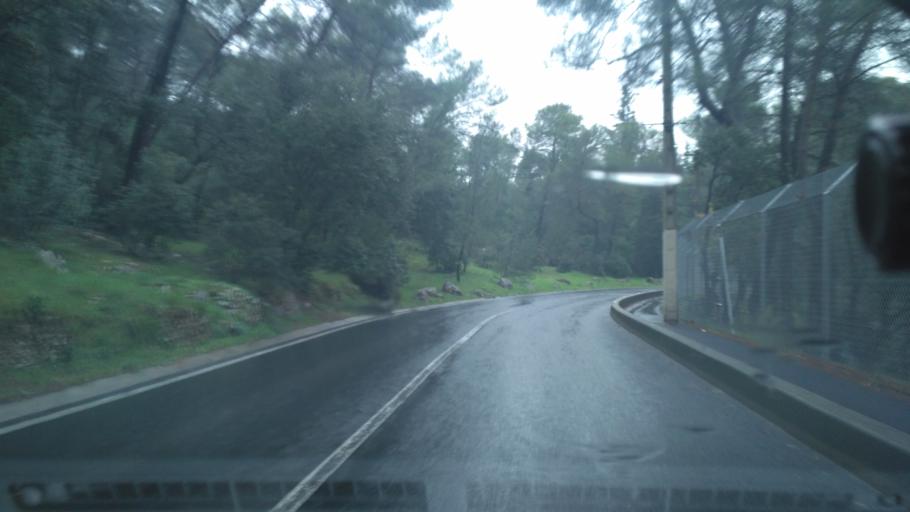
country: FR
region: Languedoc-Roussillon
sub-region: Departement de l'Herault
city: Clapiers
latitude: 43.6417
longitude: 3.8717
